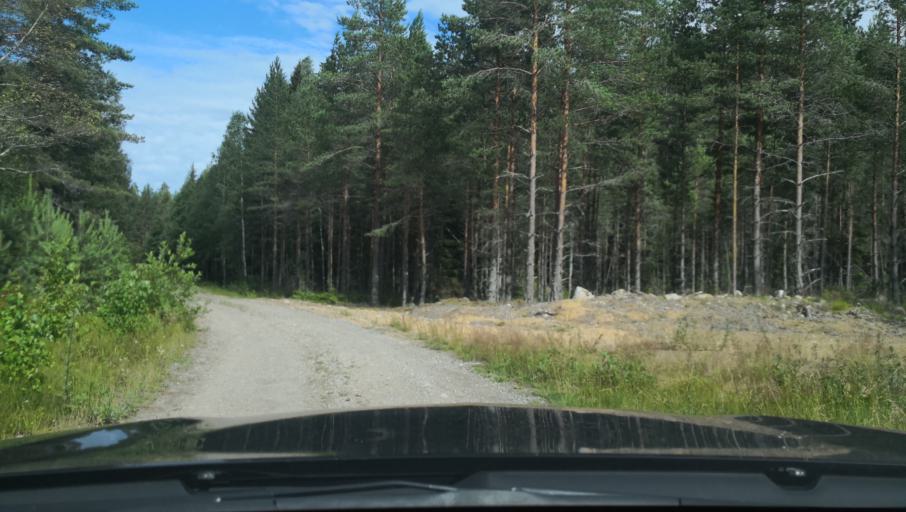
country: SE
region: Vaestmanland
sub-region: Surahammars Kommun
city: Surahammar
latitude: 59.6586
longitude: 16.0970
